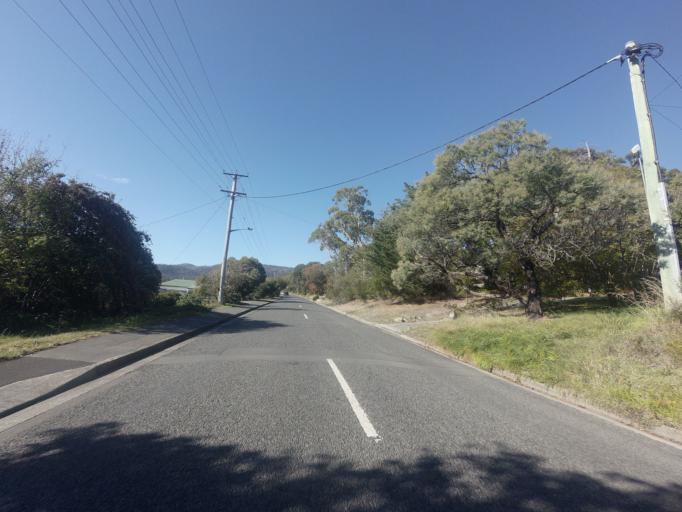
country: AU
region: Tasmania
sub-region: Clarence
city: Lindisfarne
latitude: -42.8410
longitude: 147.3451
